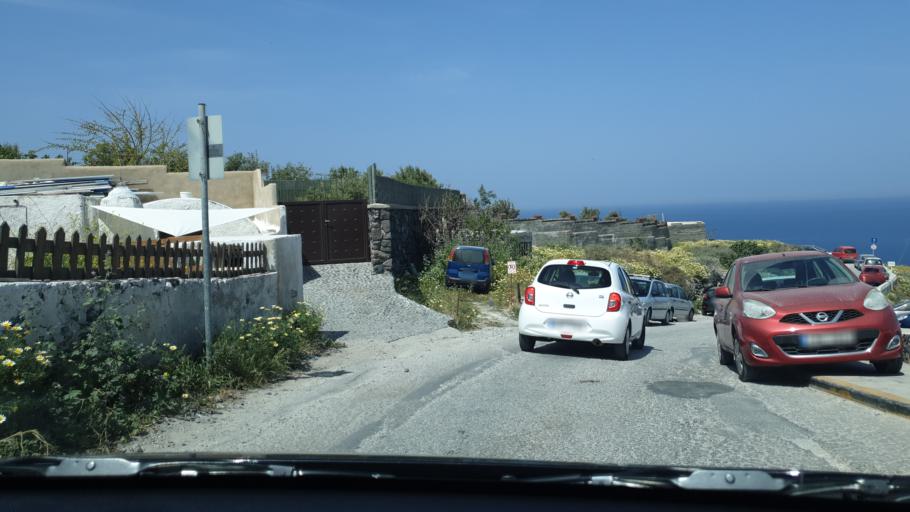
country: GR
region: South Aegean
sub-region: Nomos Kykladon
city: Oia
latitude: 36.4624
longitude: 25.3735
